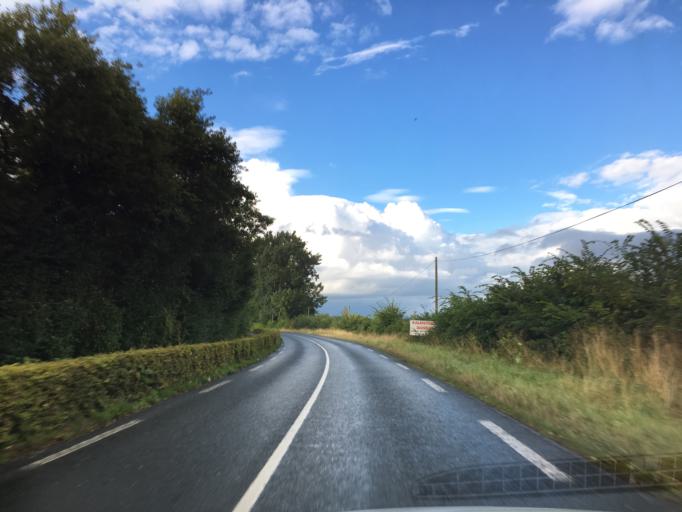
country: FR
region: Lower Normandy
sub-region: Departement du Calvados
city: Amfreville
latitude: 49.2661
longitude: -0.2220
